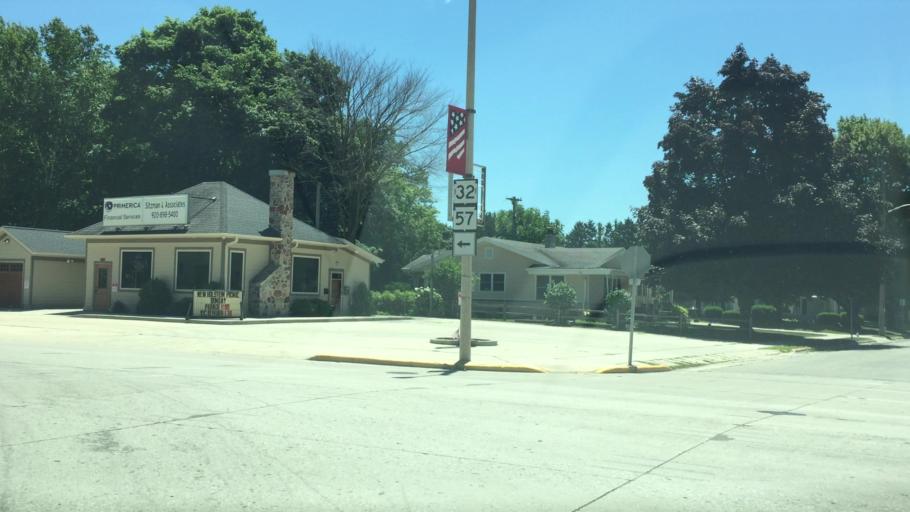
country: US
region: Wisconsin
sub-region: Calumet County
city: New Holstein
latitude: 43.9498
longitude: -88.0983
